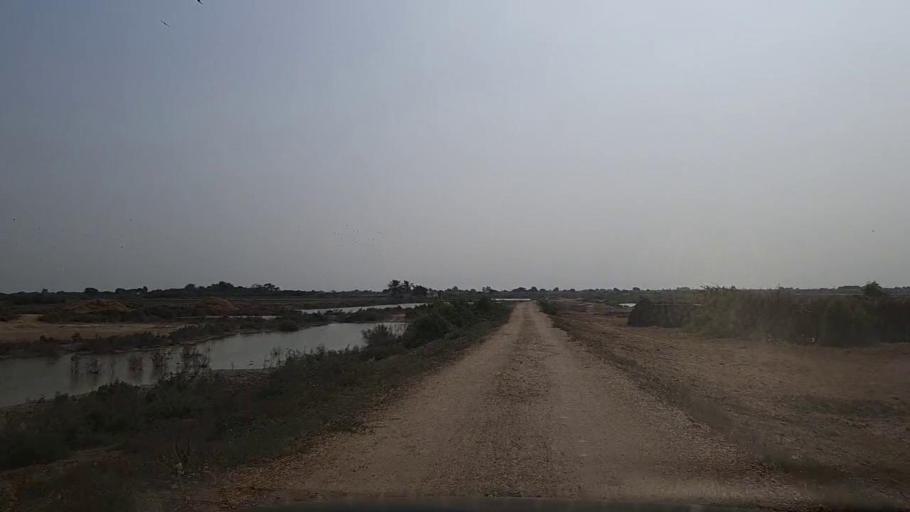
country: PK
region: Sindh
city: Thatta
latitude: 24.5719
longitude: 67.9167
